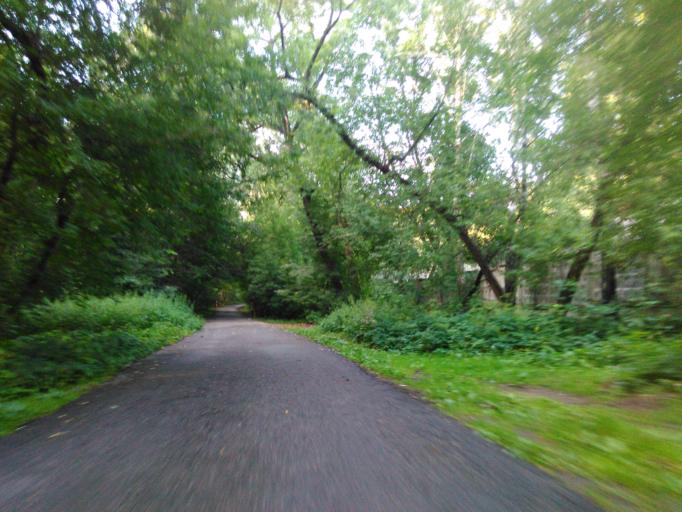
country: RU
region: Moscow
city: Sokol'niki
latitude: 55.8072
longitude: 37.6626
